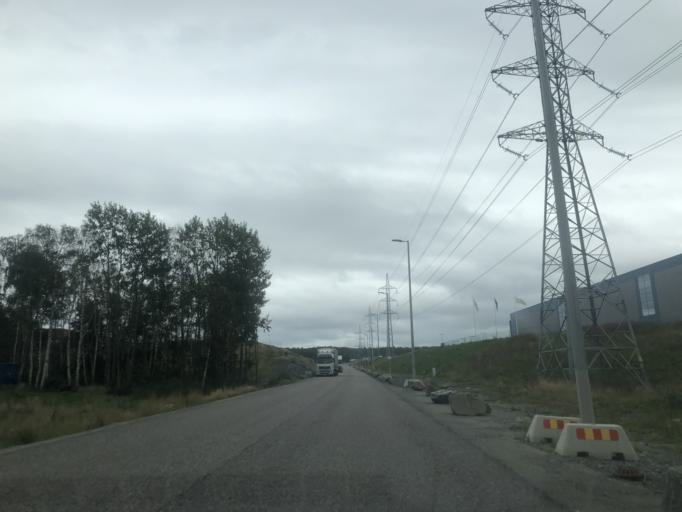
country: SE
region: Vaestra Goetaland
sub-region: Goteborg
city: Majorna
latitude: 57.7368
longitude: 11.8652
